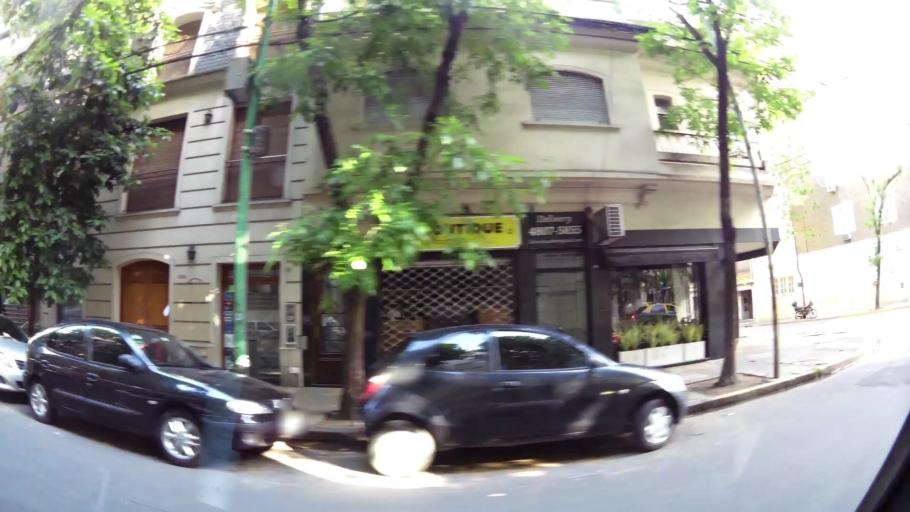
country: AR
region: Buenos Aires F.D.
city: Retiro
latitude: -34.5879
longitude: -58.4002
